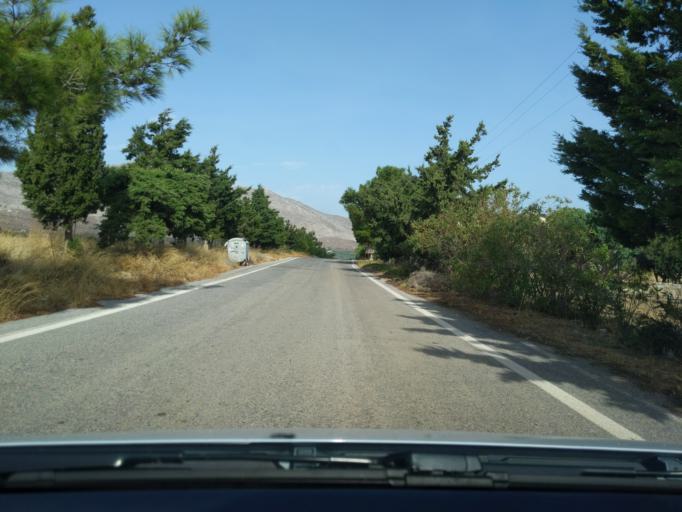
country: GR
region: Crete
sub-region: Nomos Lasithiou
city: Palekastro
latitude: 35.0915
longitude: 26.2375
